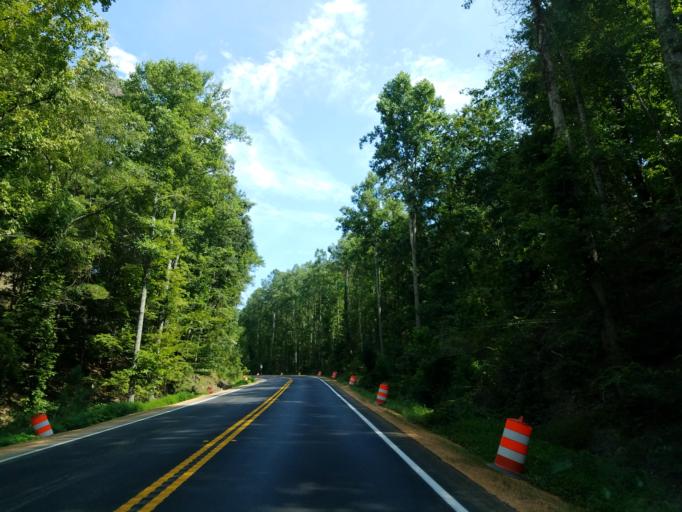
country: US
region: Georgia
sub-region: Gilmer County
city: Ellijay
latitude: 34.5807
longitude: -84.6404
